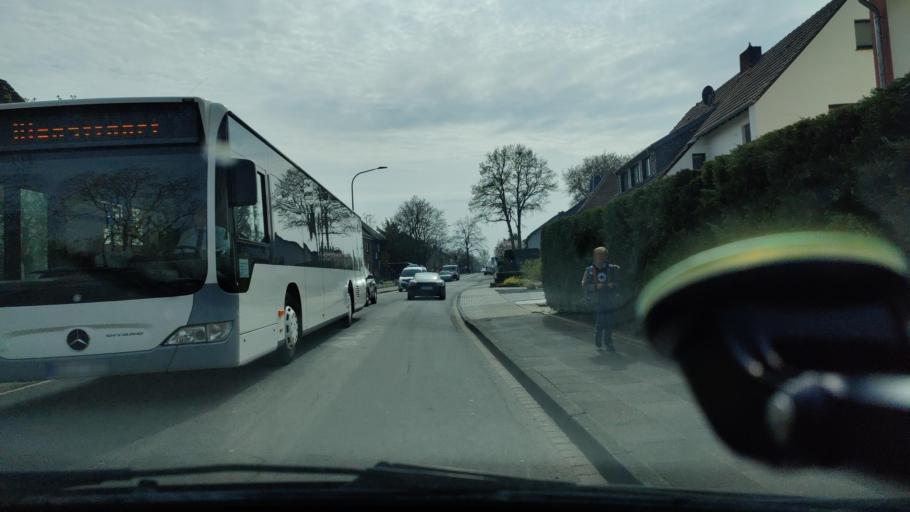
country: DE
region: North Rhine-Westphalia
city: Rheinberg
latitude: 51.5310
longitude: 6.6374
